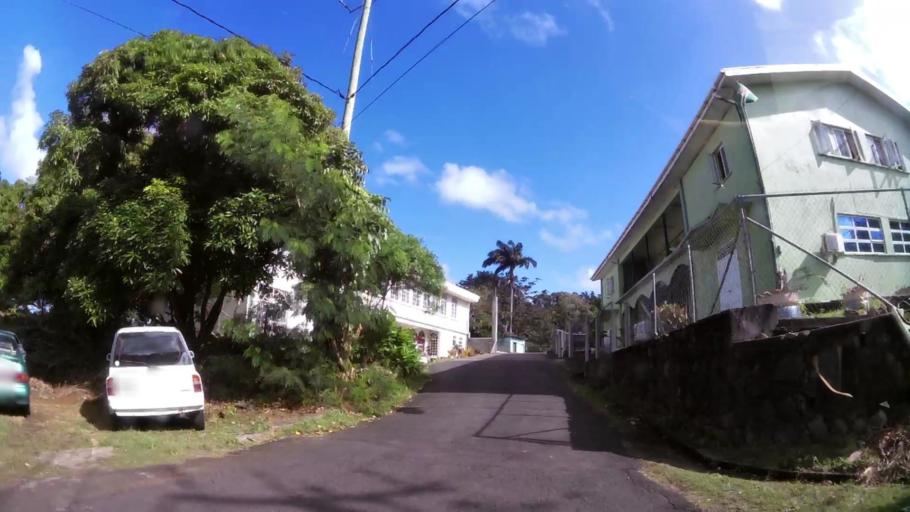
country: DM
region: Saint Andrew
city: Marigot
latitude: 15.5405
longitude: -61.2835
